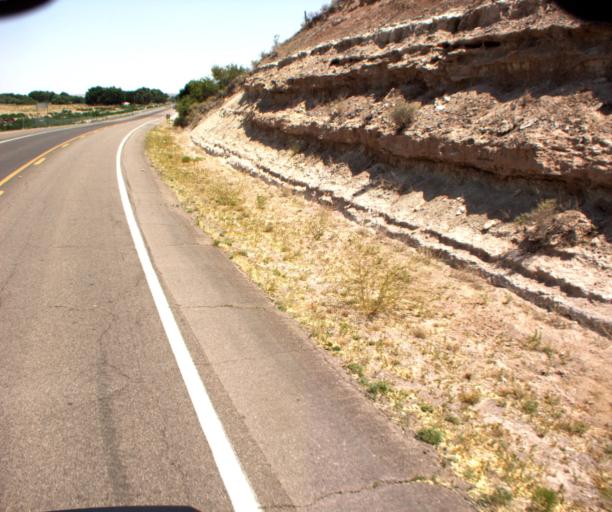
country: US
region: Arizona
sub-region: Greenlee County
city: Clifton
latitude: 32.7303
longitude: -109.1124
